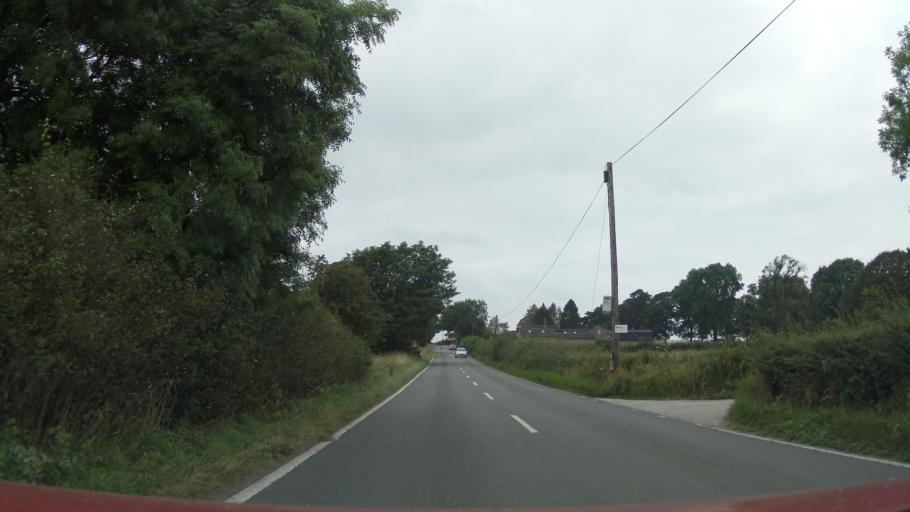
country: GB
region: England
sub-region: Derbyshire
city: Wirksworth
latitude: 53.0184
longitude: -1.5951
